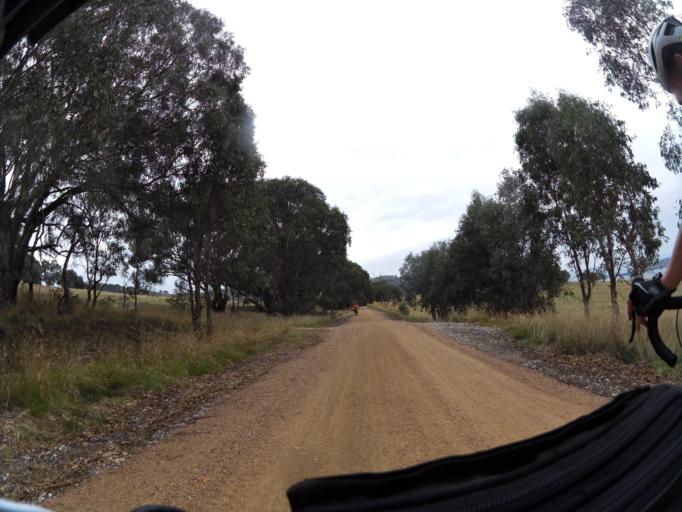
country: AU
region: New South Wales
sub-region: Albury Municipality
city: East Albury
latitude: -36.1992
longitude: 147.0431
